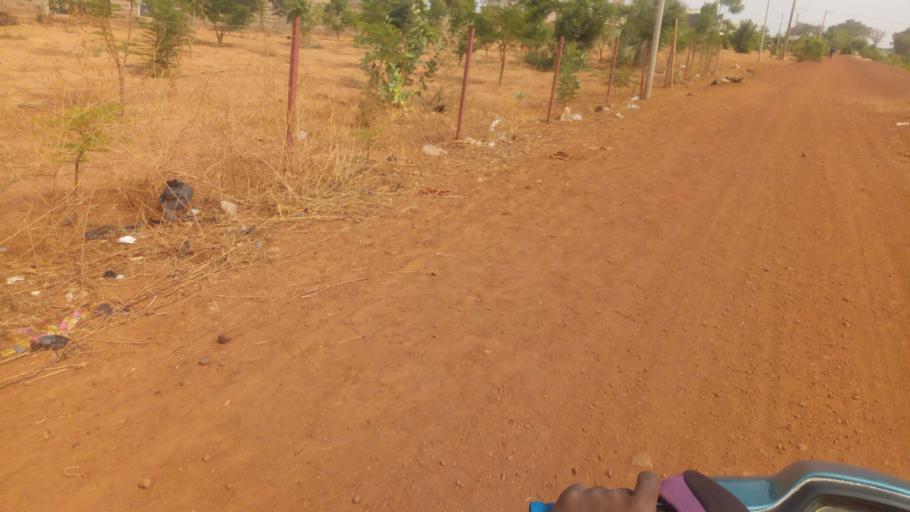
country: ML
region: Segou
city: Segou
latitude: 13.4300
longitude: -6.3014
